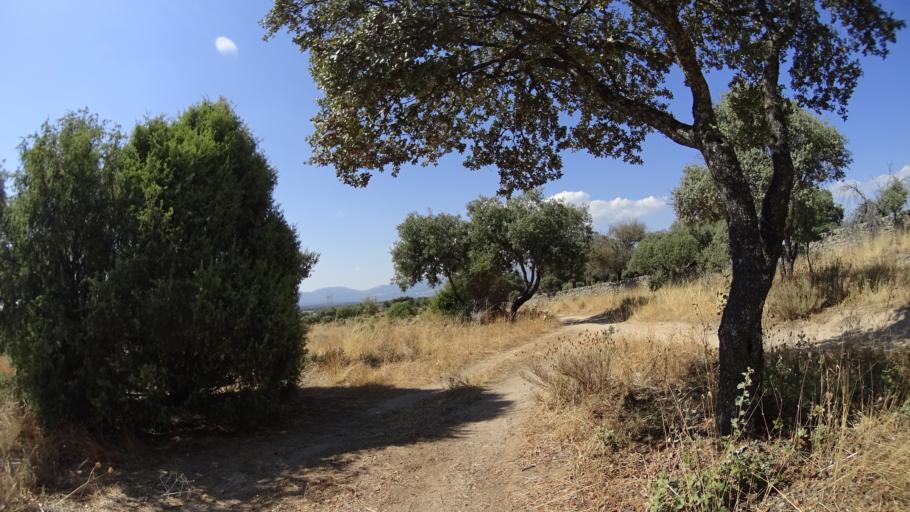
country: ES
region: Madrid
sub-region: Provincia de Madrid
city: Galapagar
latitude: 40.5999
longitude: -4.0104
